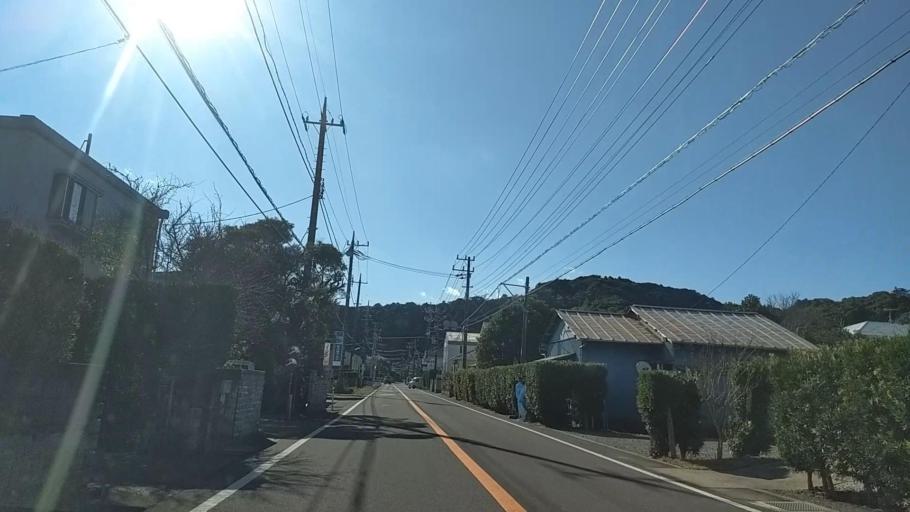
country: JP
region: Chiba
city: Tateyama
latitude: 34.9771
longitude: 139.8634
